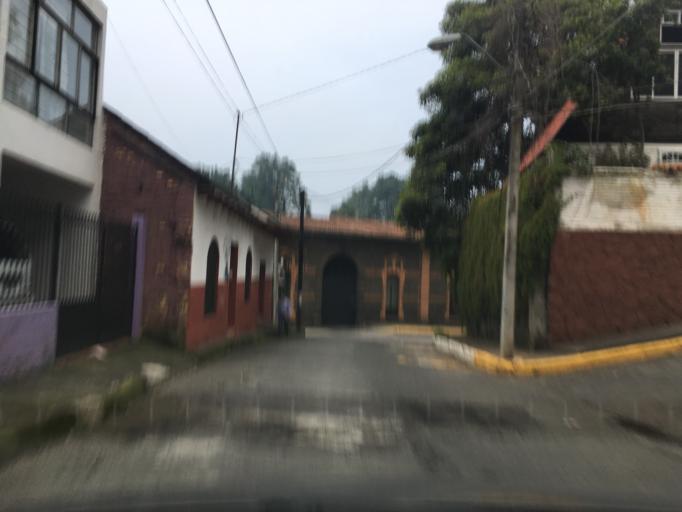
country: MX
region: Michoacan
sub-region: Uruapan
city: Uruapan
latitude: 19.4195
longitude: -102.0679
